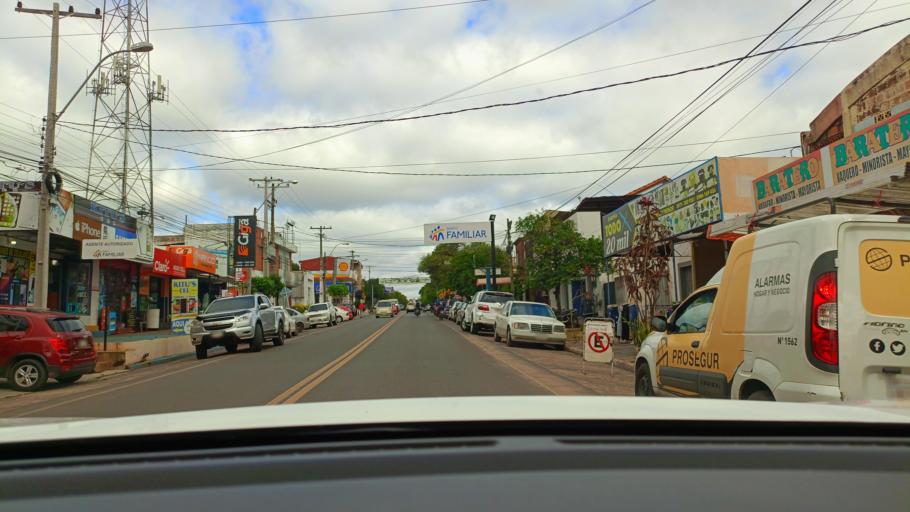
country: PY
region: San Pedro
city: Guayaybi
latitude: -24.6634
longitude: -56.4437
